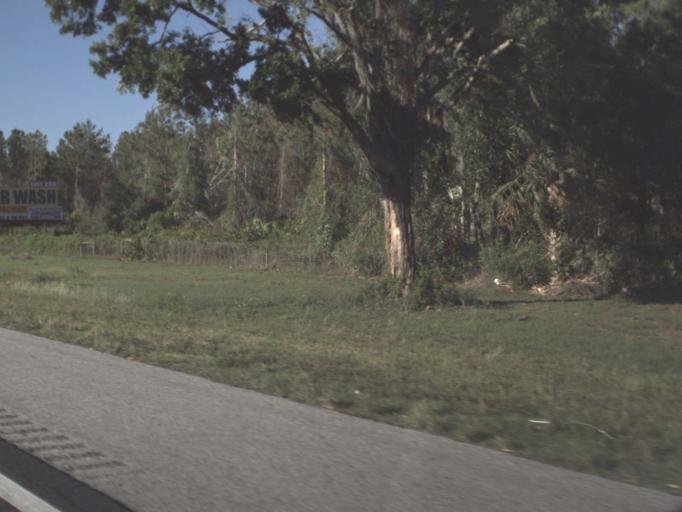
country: US
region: Florida
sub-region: Flagler County
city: Flagler Beach
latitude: 29.4911
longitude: -81.1894
